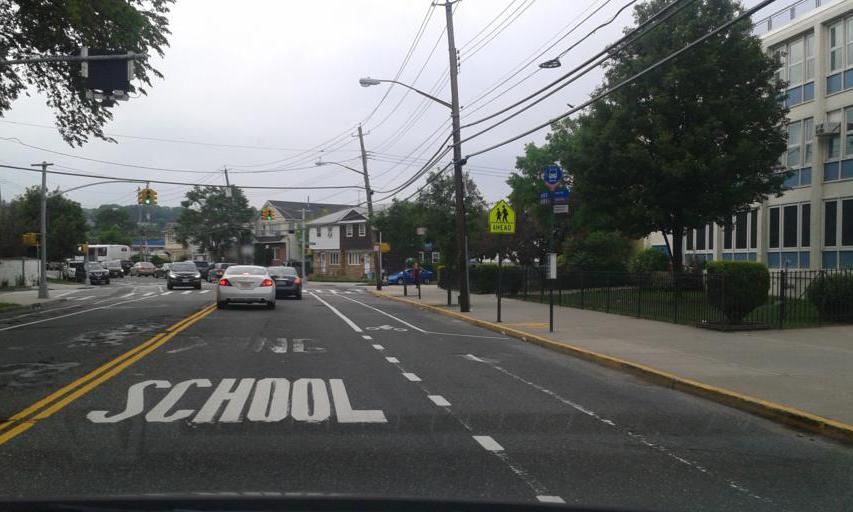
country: US
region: New York
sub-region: Richmond County
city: Staten Island
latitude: 40.5767
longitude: -74.1006
